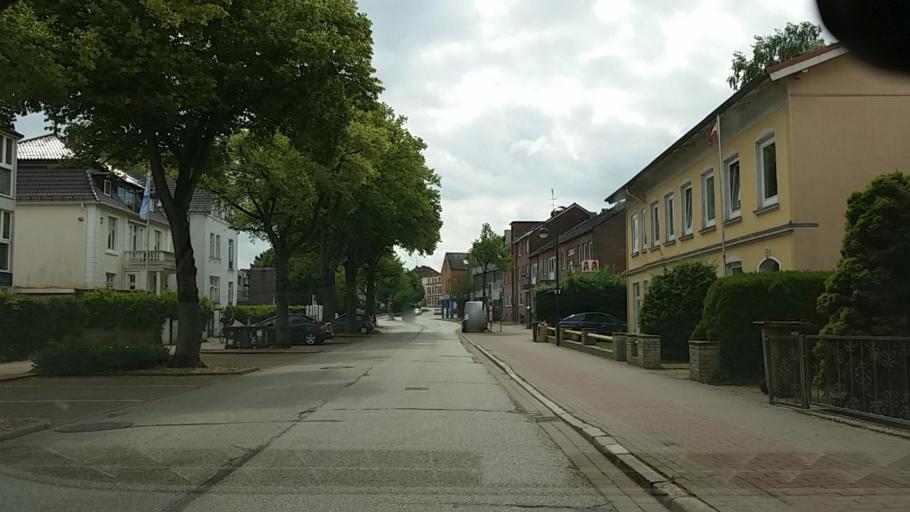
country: DE
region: Schleswig-Holstein
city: Bad Oldesloe
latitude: 53.8096
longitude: 10.3680
